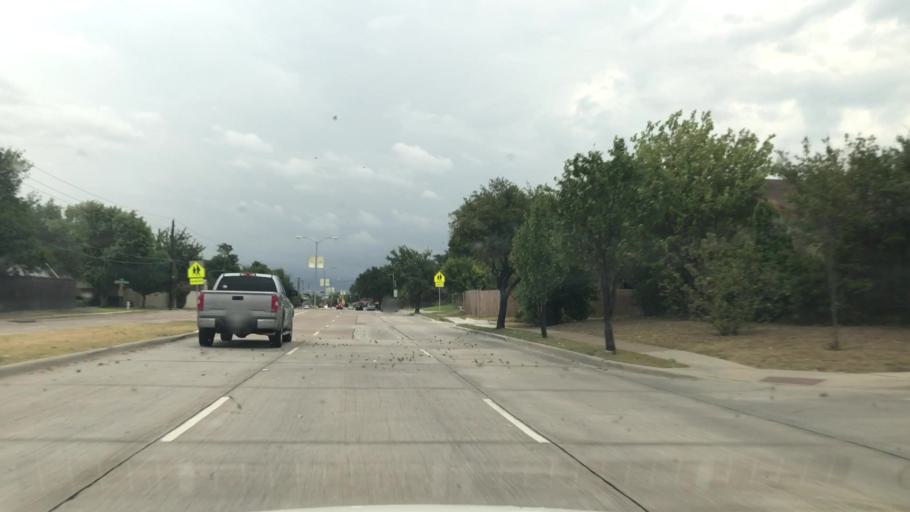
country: US
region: Texas
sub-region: Dallas County
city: Carrollton
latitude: 32.9977
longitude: -96.8763
